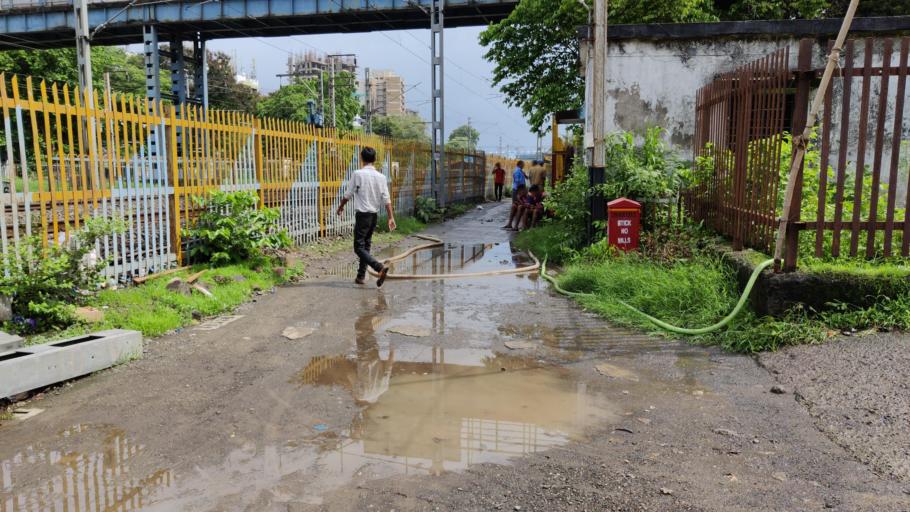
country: IN
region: Maharashtra
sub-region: Mumbai Suburban
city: Borivli
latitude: 19.2467
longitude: 72.8596
